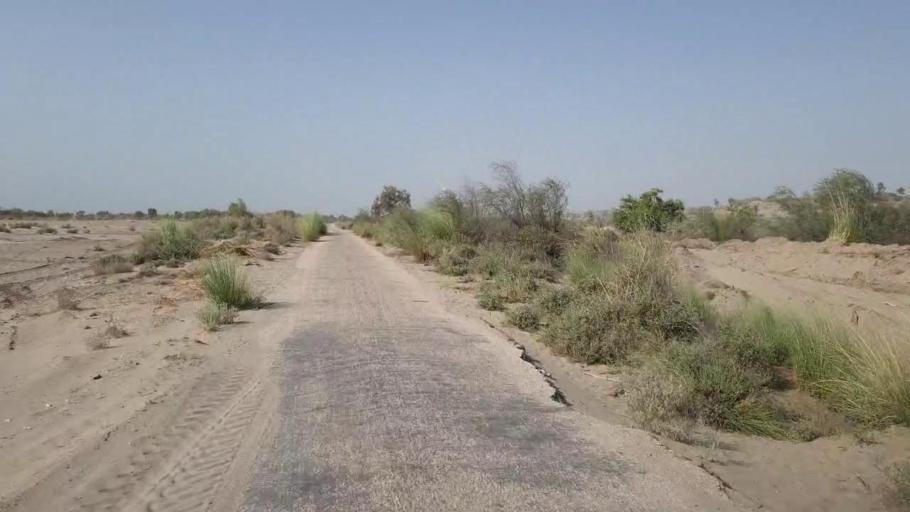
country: PK
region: Sindh
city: Jam Sahib
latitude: 26.6009
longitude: 68.9255
